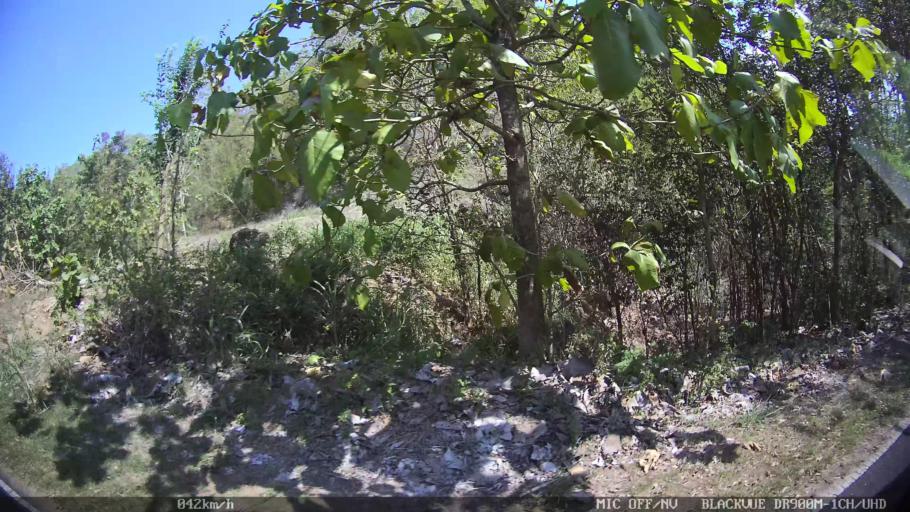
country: ID
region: Daerah Istimewa Yogyakarta
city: Pundong
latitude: -7.9570
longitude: 110.3656
